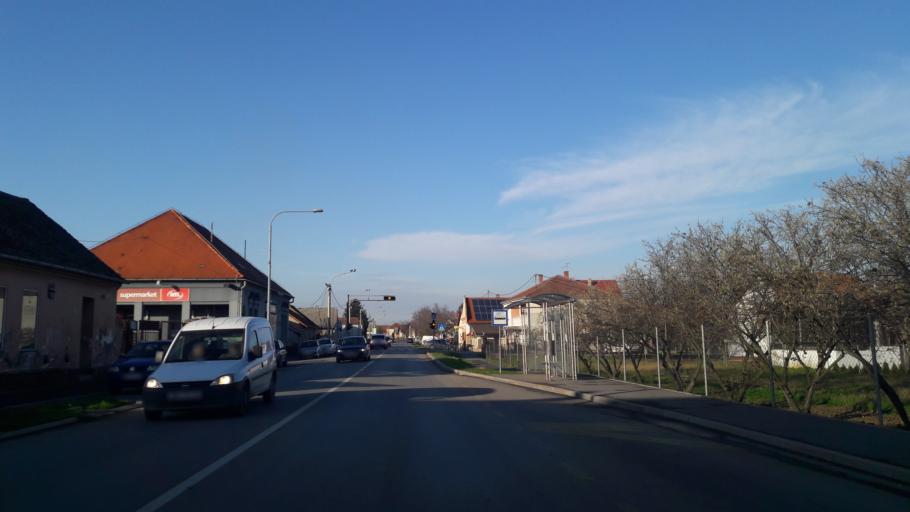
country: HR
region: Osjecko-Baranjska
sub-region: Grad Osijek
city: Bilje
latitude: 45.6048
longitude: 18.7434
